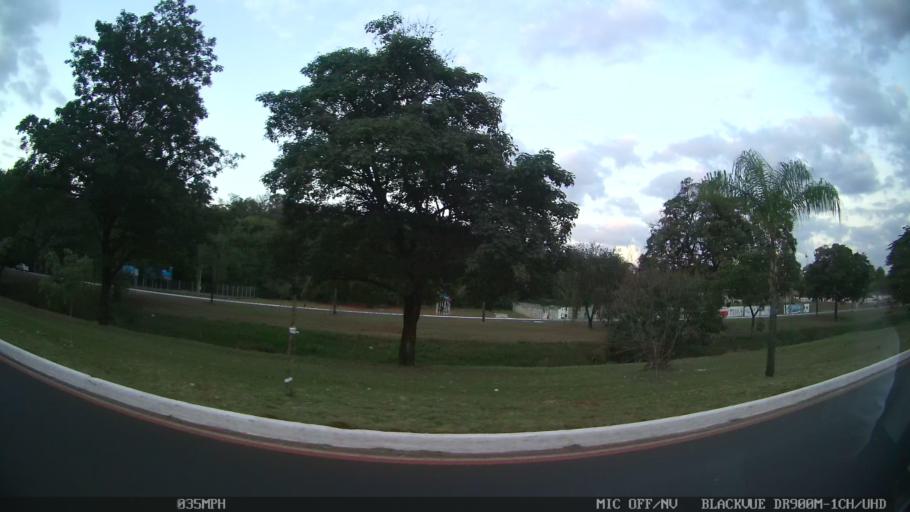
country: BR
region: Sao Paulo
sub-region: Ribeirao Preto
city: Ribeirao Preto
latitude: -21.2017
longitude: -47.7950
